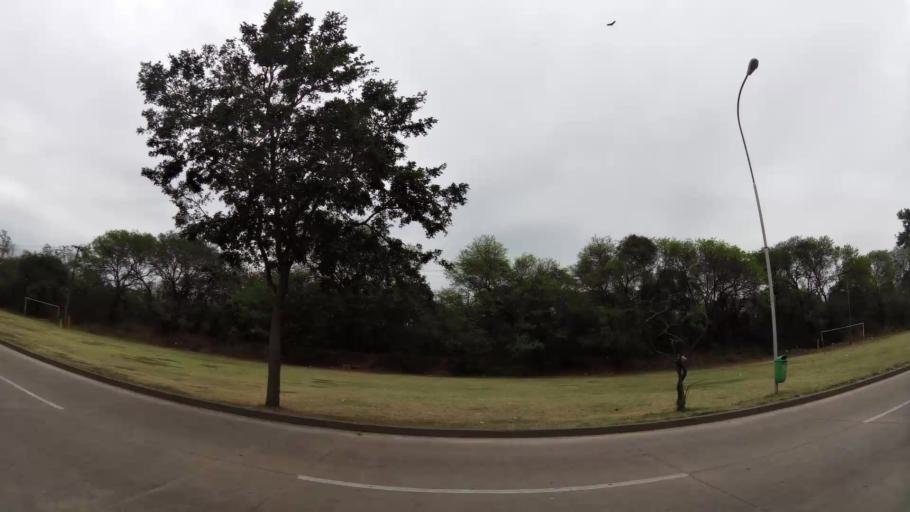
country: BO
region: Santa Cruz
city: Santa Cruz de la Sierra
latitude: -17.7745
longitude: -63.2144
